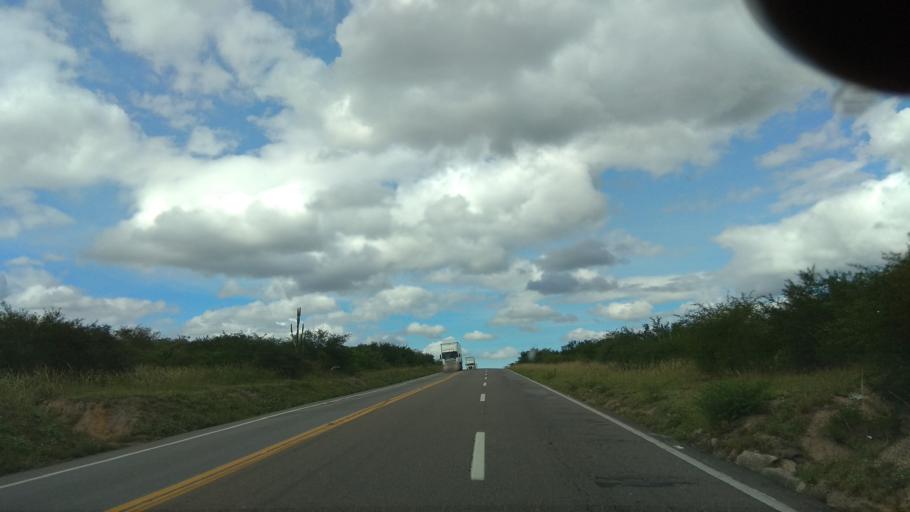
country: BR
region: Bahia
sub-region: Amargosa
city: Amargosa
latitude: -12.9341
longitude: -39.8962
